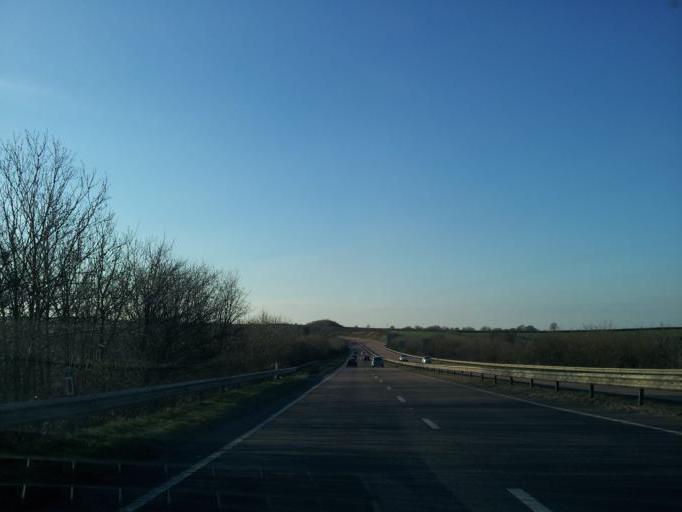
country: GB
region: England
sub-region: Devon
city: Okehampton
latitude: 50.7233
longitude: -3.8521
